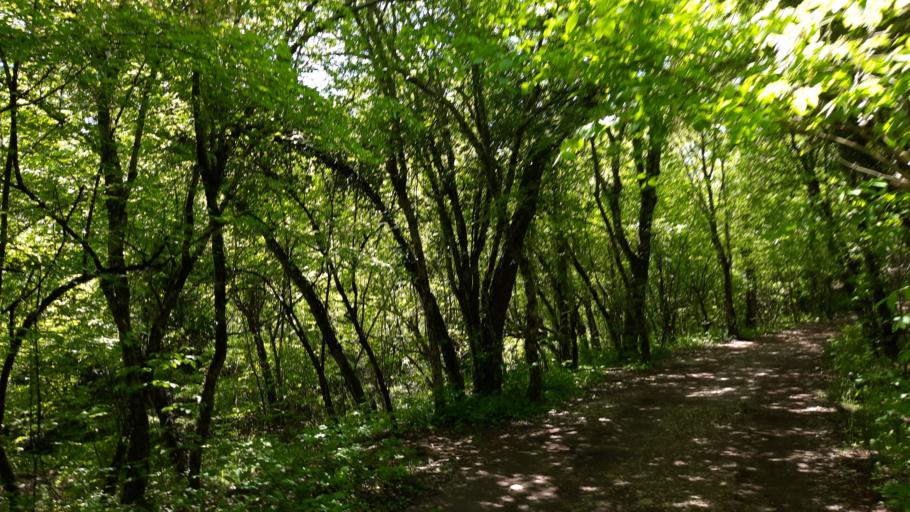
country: RU
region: Krasnodarskiy
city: Divnomorskoye
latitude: 44.5628
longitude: 38.2589
